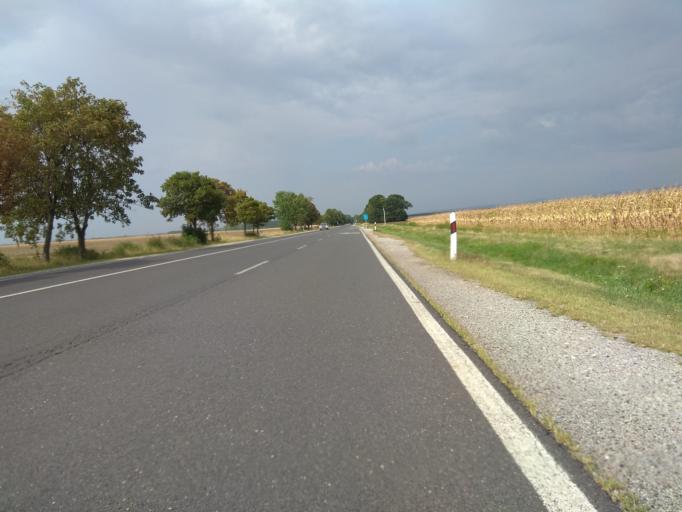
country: HU
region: Borsod-Abauj-Zemplen
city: Emod
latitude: 47.9300
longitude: 20.8003
